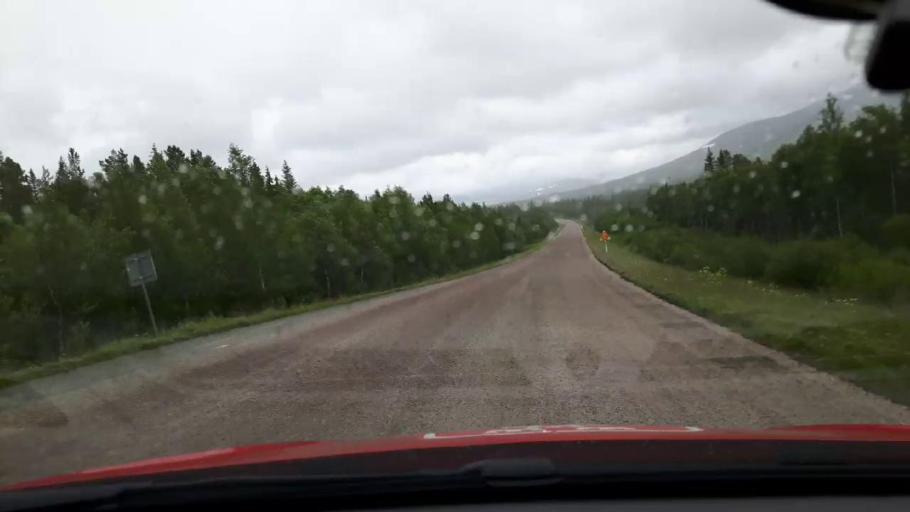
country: NO
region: Nord-Trondelag
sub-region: Meraker
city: Meraker
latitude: 63.2840
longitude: 12.3499
